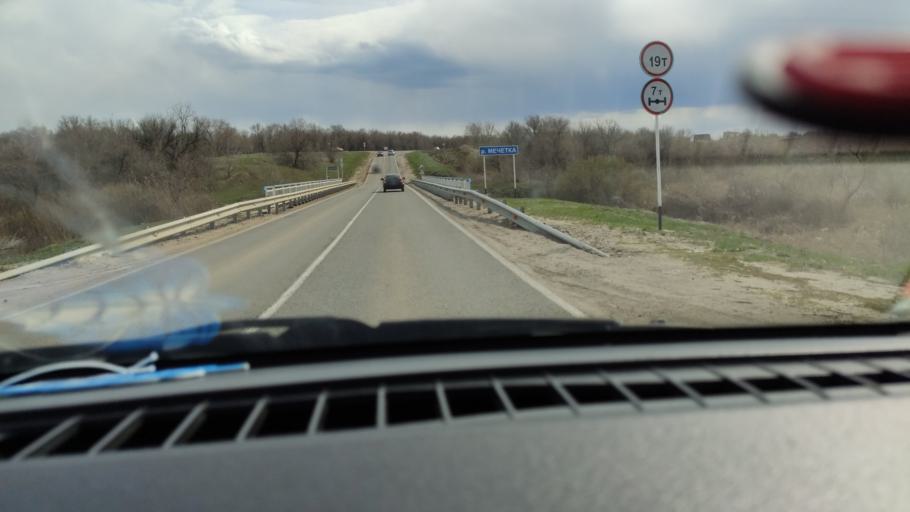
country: RU
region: Saratov
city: Privolzhskiy
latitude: 51.3454
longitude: 46.0435
